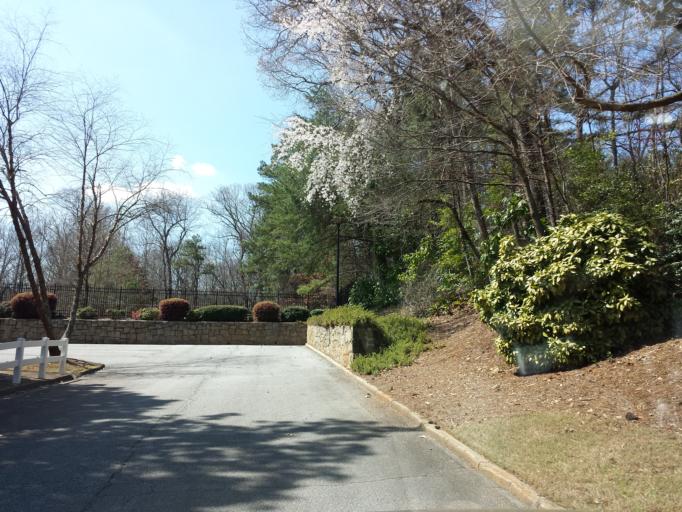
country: US
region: Georgia
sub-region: Cobb County
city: Vinings
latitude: 33.9119
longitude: -84.4691
